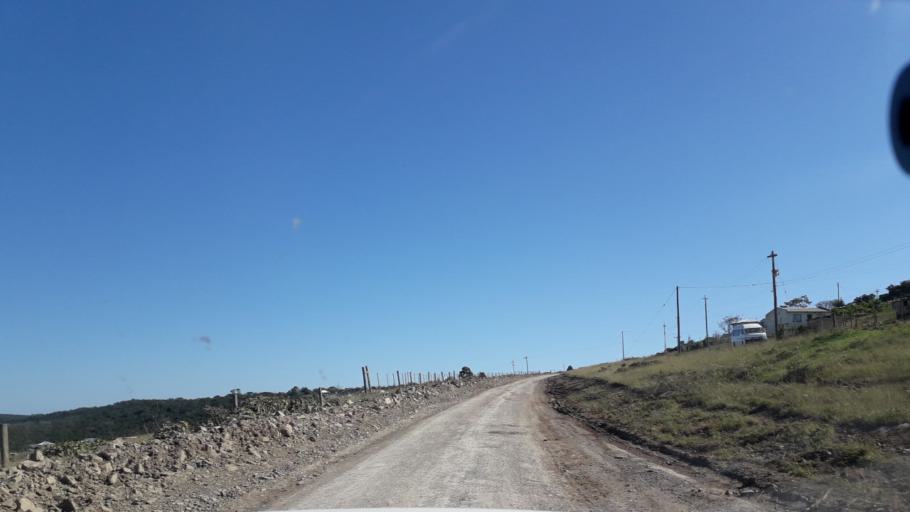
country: ZA
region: Eastern Cape
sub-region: Buffalo City Metropolitan Municipality
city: East London
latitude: -32.8249
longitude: 27.9720
